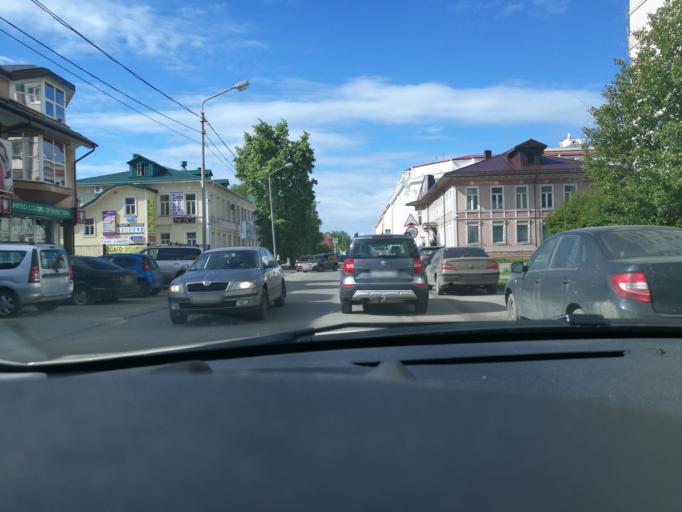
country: RU
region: Arkhangelskaya
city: Arkhangel'sk
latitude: 64.5365
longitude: 40.5277
